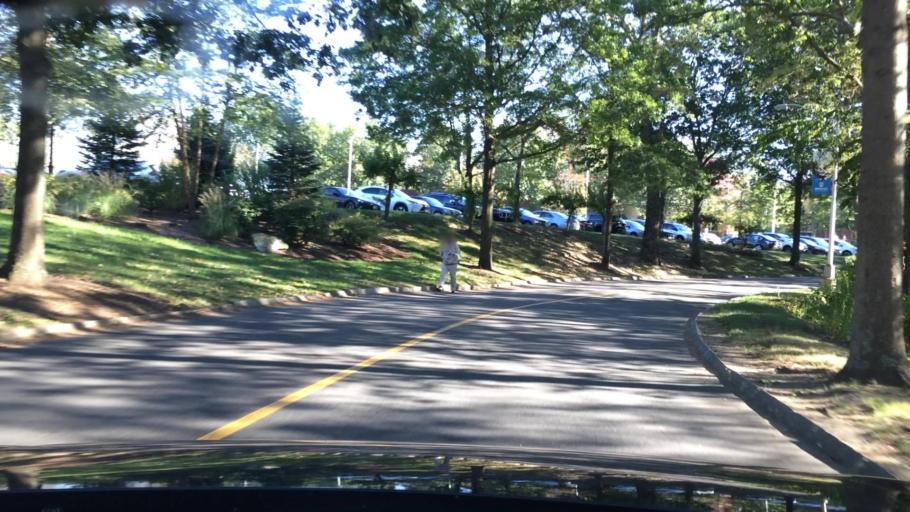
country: US
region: Massachusetts
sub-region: Middlesex County
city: Waltham
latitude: 42.3903
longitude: -71.2214
